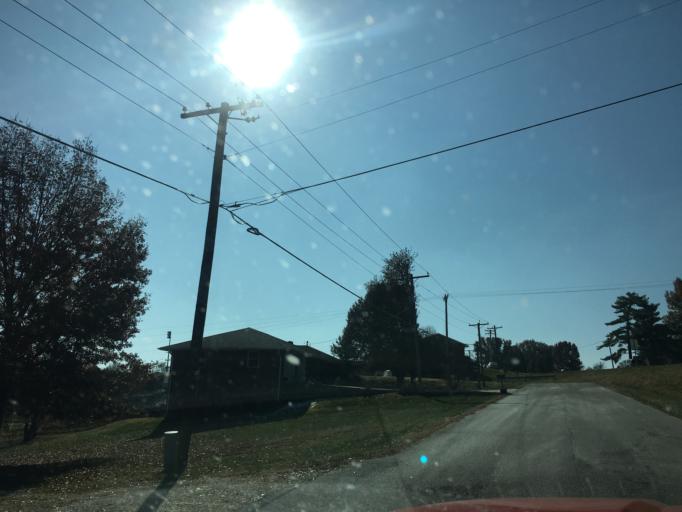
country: US
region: Missouri
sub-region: Cole County
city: Wardsville
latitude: 38.4975
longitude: -92.1774
